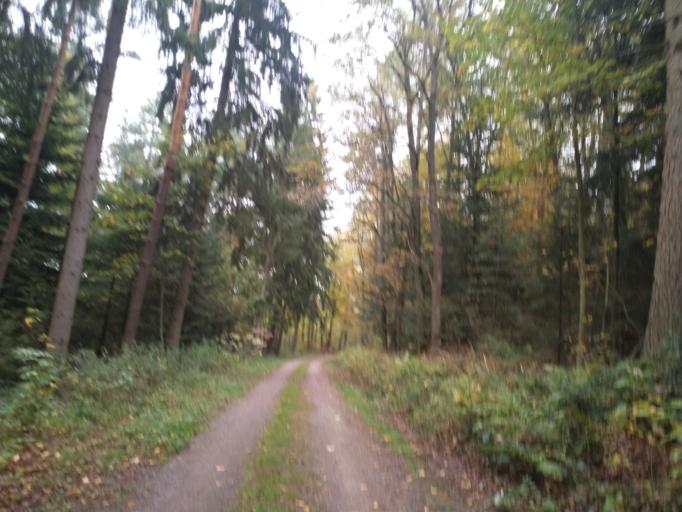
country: DE
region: Baden-Wuerttemberg
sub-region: Karlsruhe Region
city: Birkenfeld
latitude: 48.8604
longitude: 8.6462
